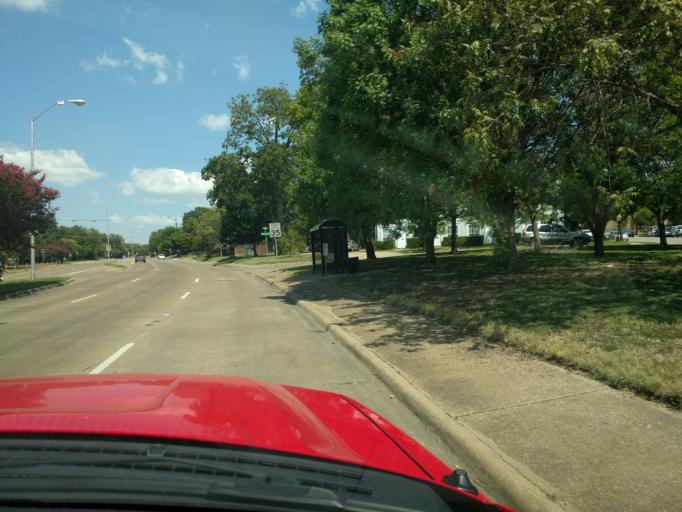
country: US
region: Texas
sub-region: Dallas County
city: Highland Park
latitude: 32.8017
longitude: -96.7560
